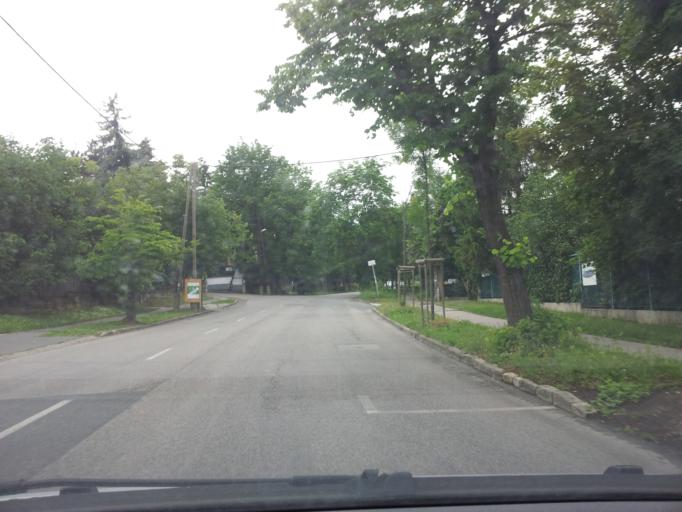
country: HU
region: Budapest
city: Budapest XII. keruelet
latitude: 47.5118
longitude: 18.9972
